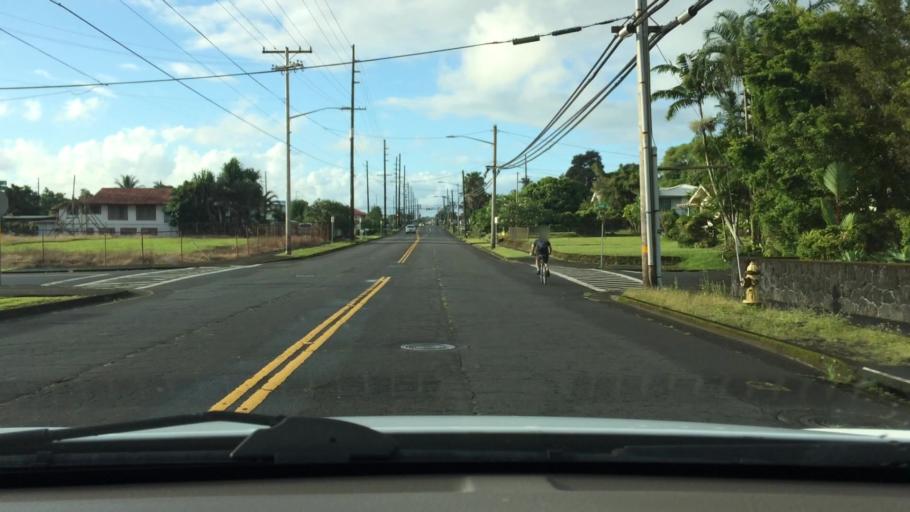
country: US
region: Hawaii
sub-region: Hawaii County
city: Hilo
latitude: 19.7081
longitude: -155.0781
